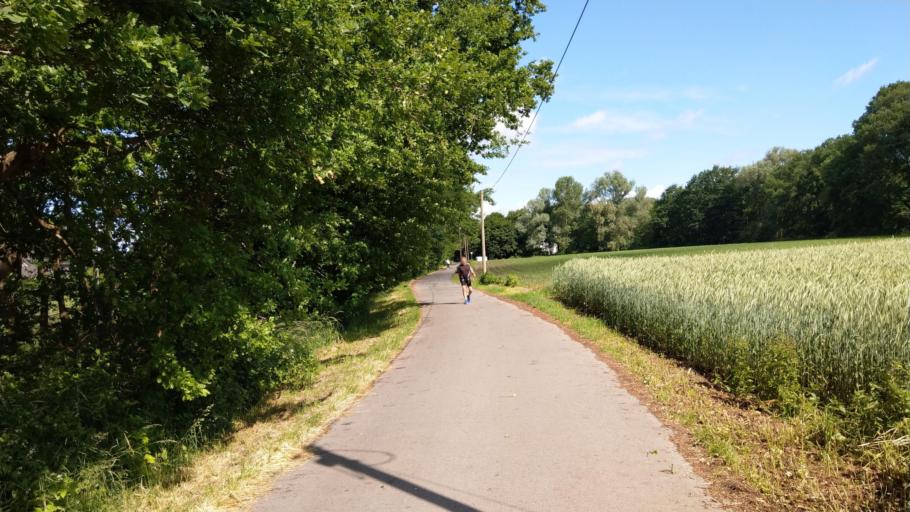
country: DE
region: North Rhine-Westphalia
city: Oer-Erkenschwick
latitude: 51.5876
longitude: 7.2586
